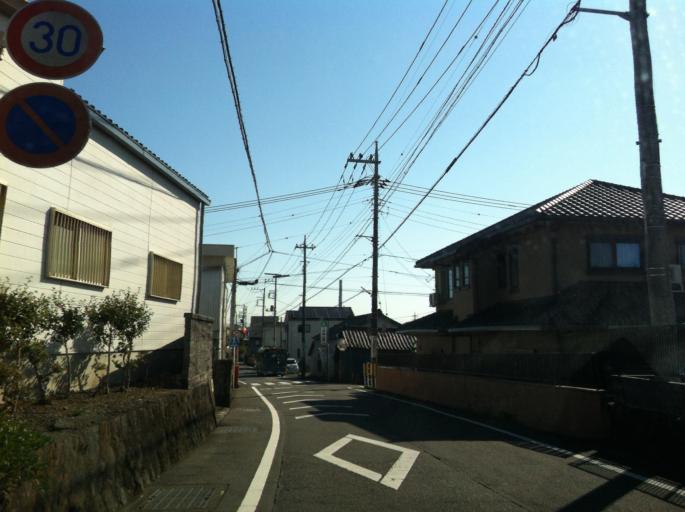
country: JP
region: Shizuoka
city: Fuji
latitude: 35.1585
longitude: 138.7482
